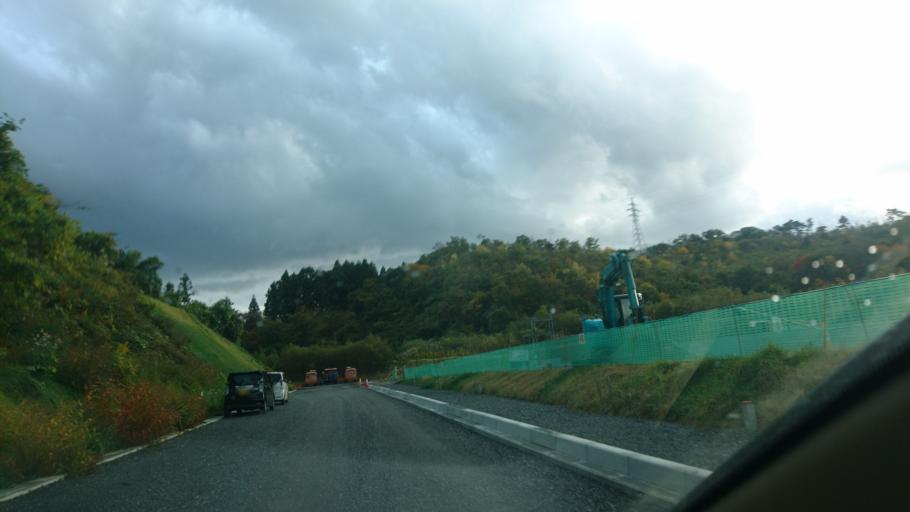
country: JP
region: Iwate
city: Ichinoseki
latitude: 38.9615
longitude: 141.1176
